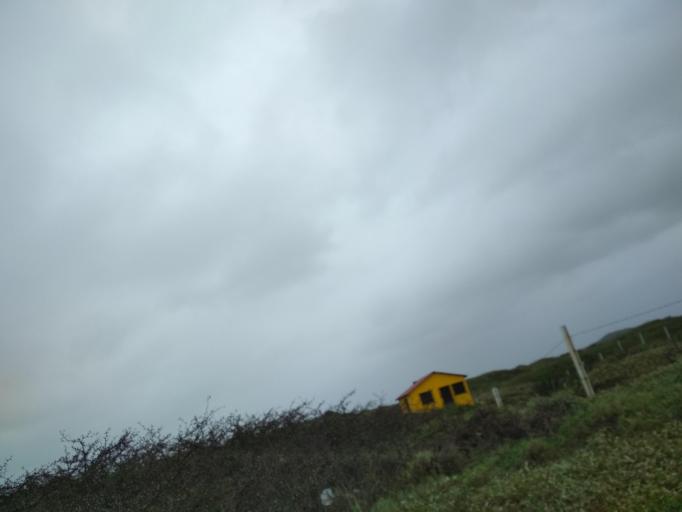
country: MX
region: Veracruz
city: Anton Lizardo
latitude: 19.0579
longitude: -96.0041
